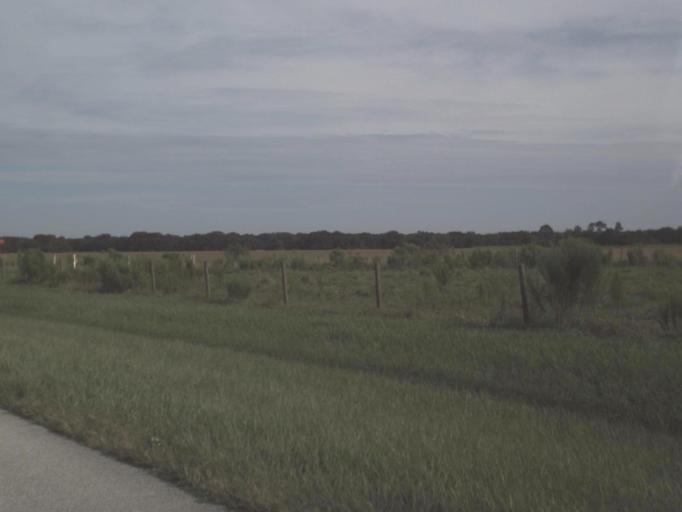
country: US
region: Florida
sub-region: DeSoto County
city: Nocatee
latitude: 27.0443
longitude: -81.7790
